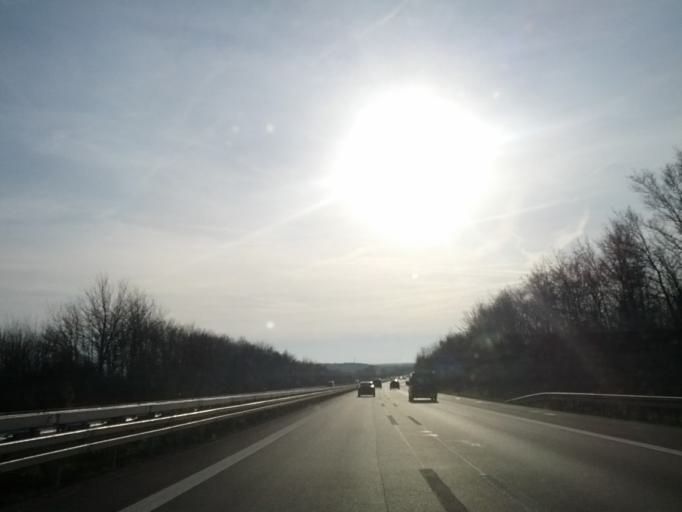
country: DE
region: Bavaria
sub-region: Regierungsbezirk Unterfranken
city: Biebelried
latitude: 49.7535
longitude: 10.1071
